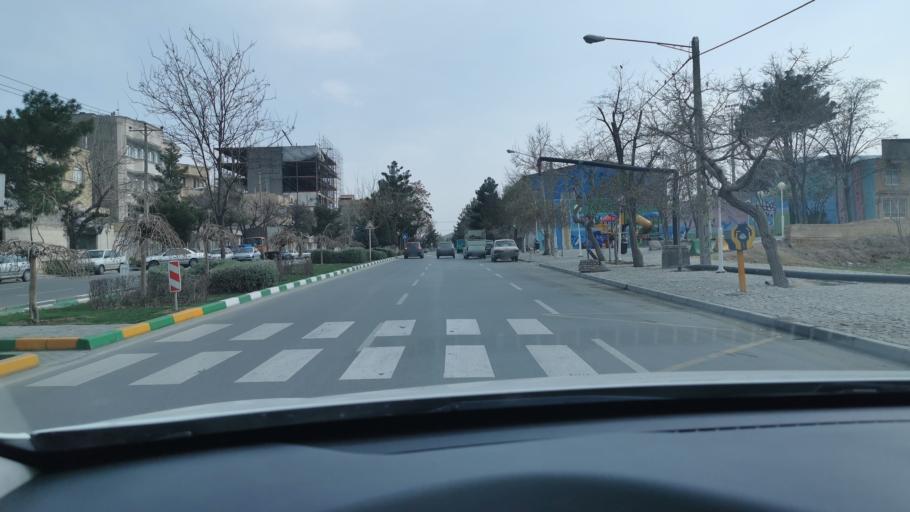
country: IR
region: Razavi Khorasan
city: Mashhad
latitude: 36.2794
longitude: 59.5646
